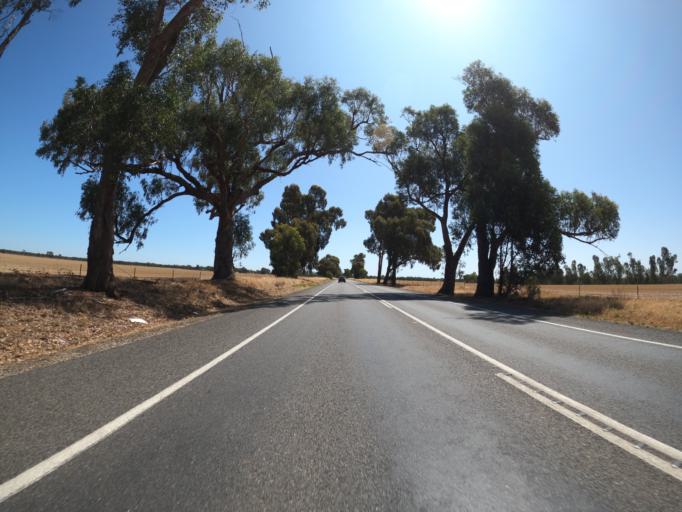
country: AU
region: Victoria
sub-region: Moira
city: Yarrawonga
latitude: -36.0223
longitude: 146.1367
